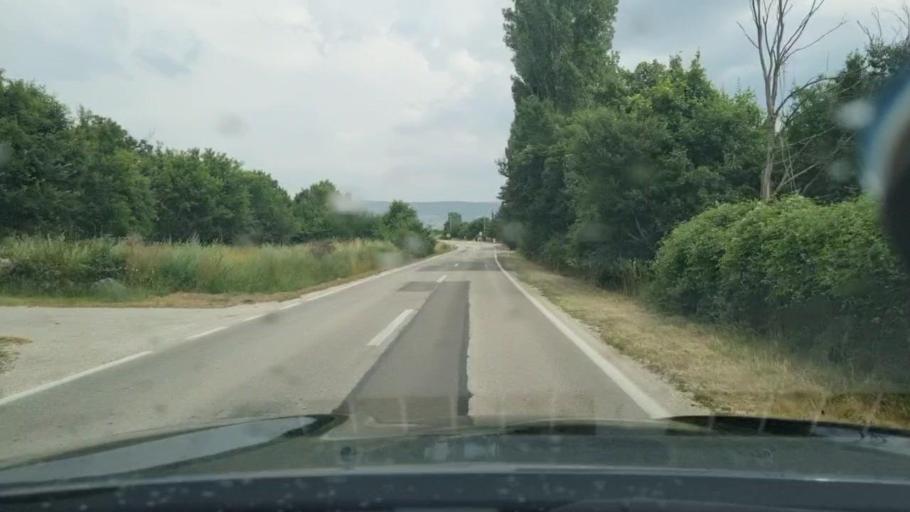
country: BA
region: Federation of Bosnia and Herzegovina
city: Podhum
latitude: 43.6880
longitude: 17.0642
